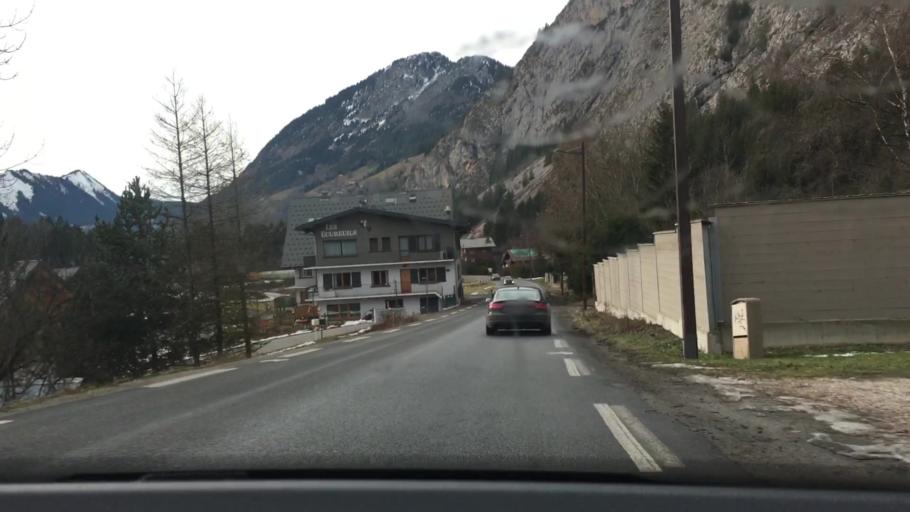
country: FR
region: Rhone-Alpes
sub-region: Departement de la Haute-Savoie
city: Abondance
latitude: 46.2949
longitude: 6.7727
